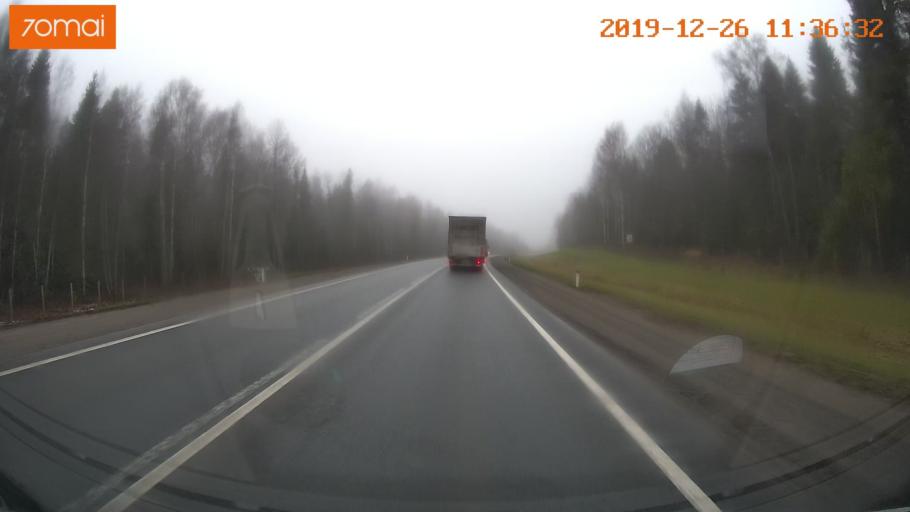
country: RU
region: Vologda
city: Sheksna
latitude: 59.1939
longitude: 38.6454
